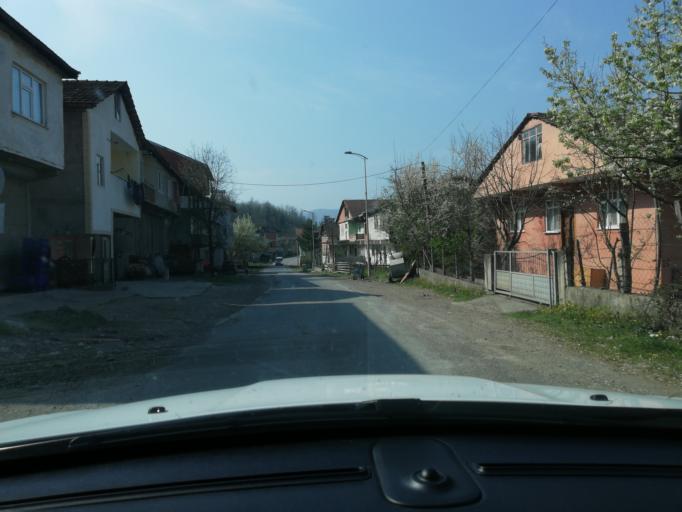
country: TR
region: Karabuk
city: Yenice
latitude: 41.2603
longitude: 32.3629
